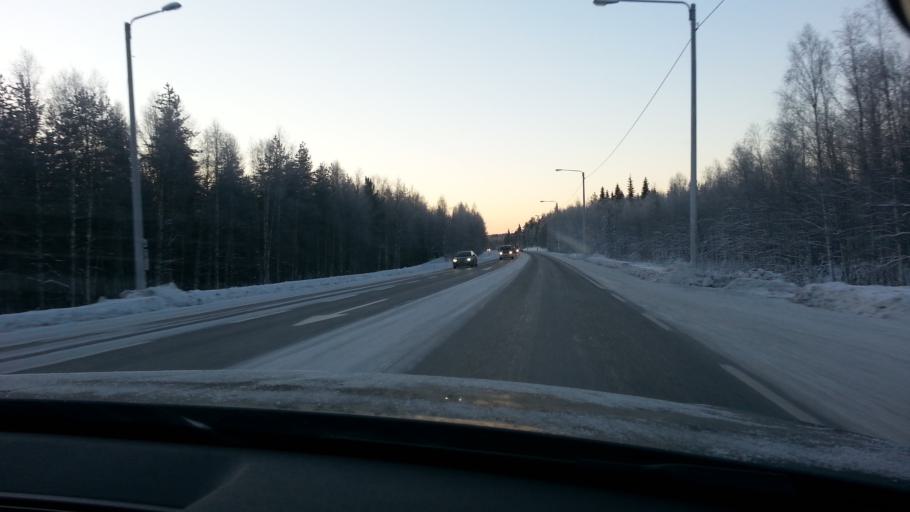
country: FI
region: Lapland
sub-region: Rovaniemi
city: Rovaniemi
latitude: 66.5340
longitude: 25.7725
